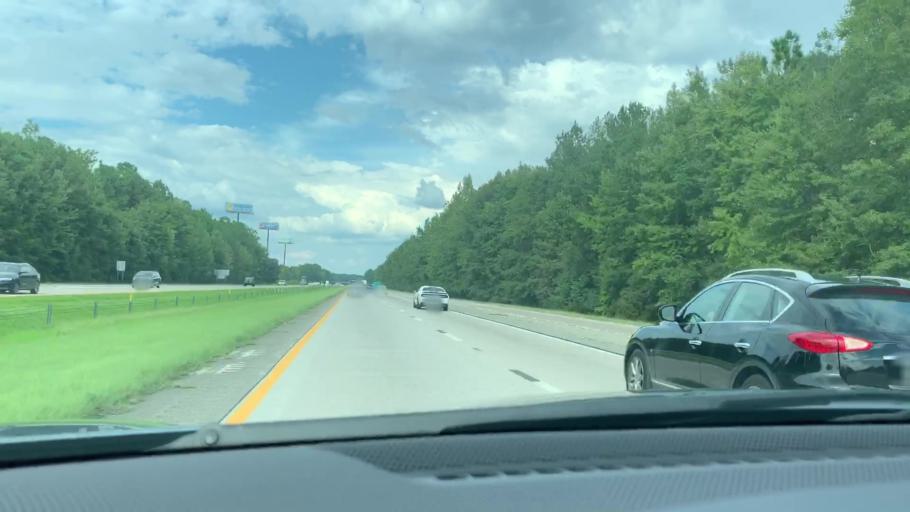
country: US
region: South Carolina
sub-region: Jasper County
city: Ridgeland
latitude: 32.4323
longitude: -80.9999
